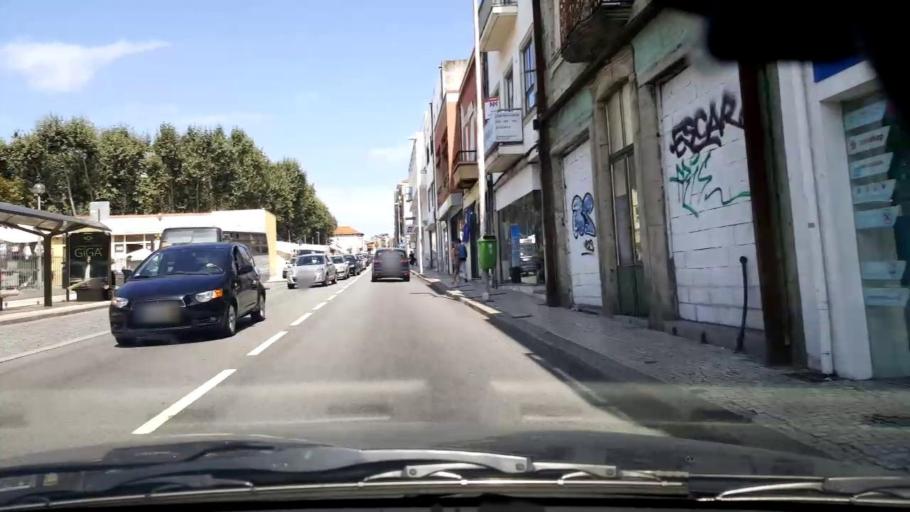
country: PT
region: Porto
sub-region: Vila do Conde
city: Vila do Conde
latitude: 41.3543
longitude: -8.7412
